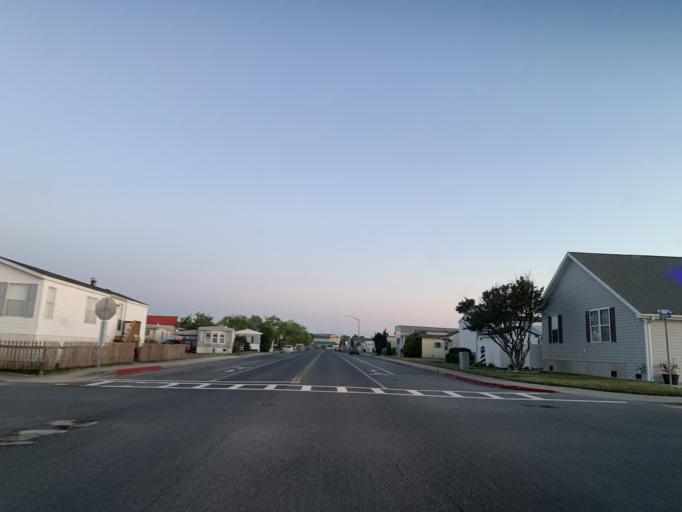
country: US
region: Delaware
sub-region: Sussex County
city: Bethany Beach
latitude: 38.4387
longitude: -75.0554
